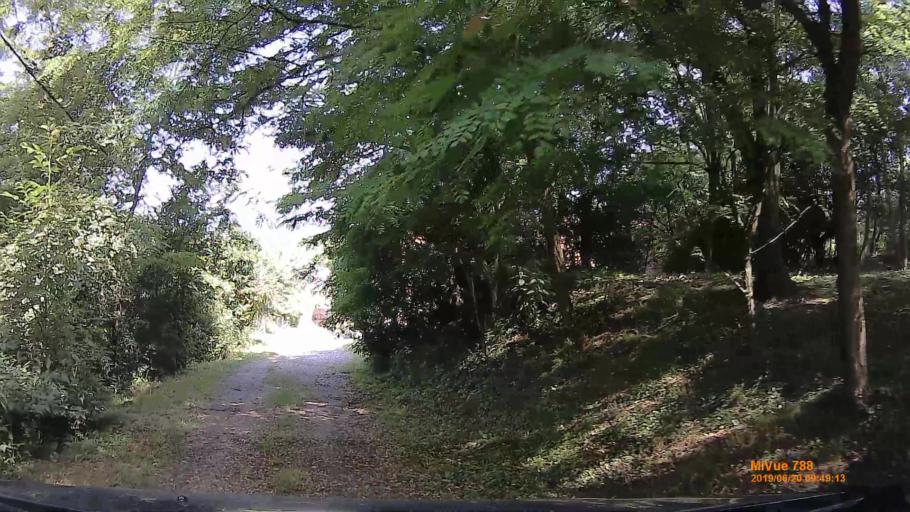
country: HU
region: Baranya
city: Pecsvarad
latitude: 46.1720
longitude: 18.4745
